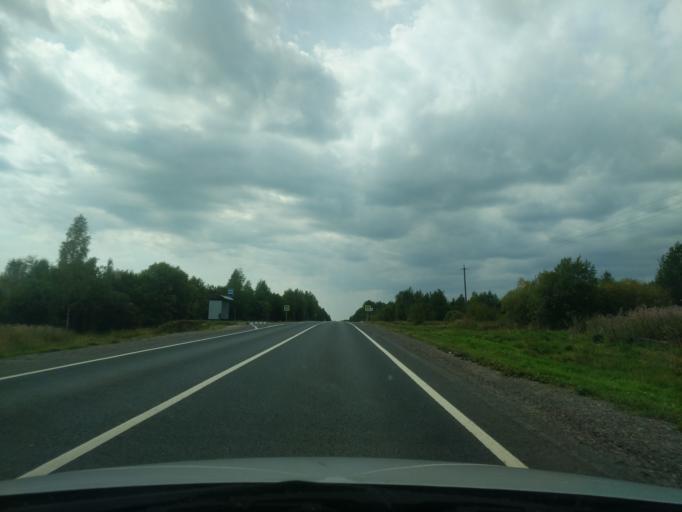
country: RU
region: Kostroma
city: Manturovo
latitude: 58.1620
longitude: 44.3974
